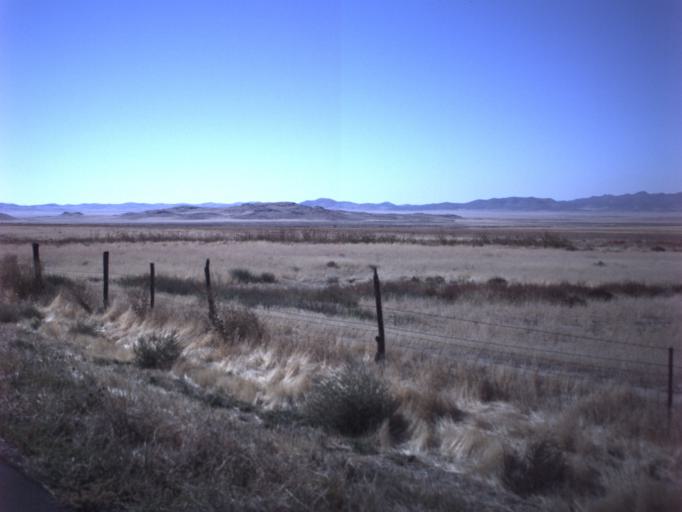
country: US
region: Utah
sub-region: Tooele County
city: Grantsville
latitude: 40.4242
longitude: -112.7488
